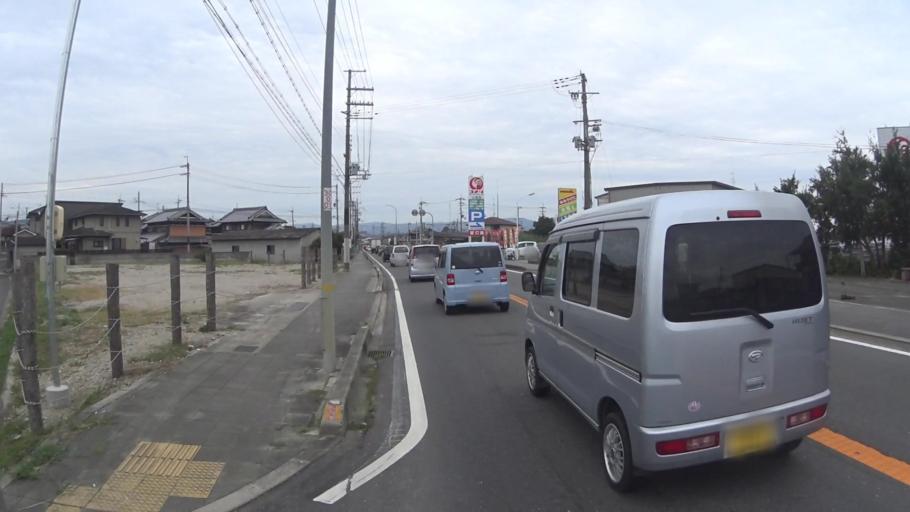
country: JP
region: Nara
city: Nara-shi
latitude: 34.7515
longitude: 135.8155
